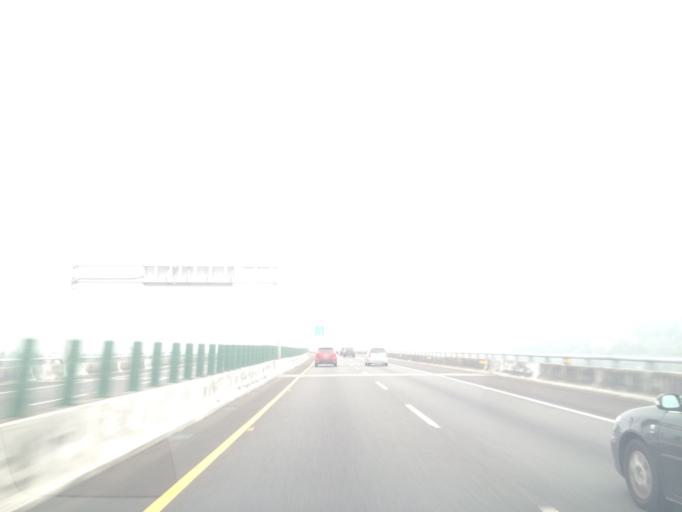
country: TW
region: Taiwan
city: Zhongxing New Village
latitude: 24.0092
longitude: 120.7045
